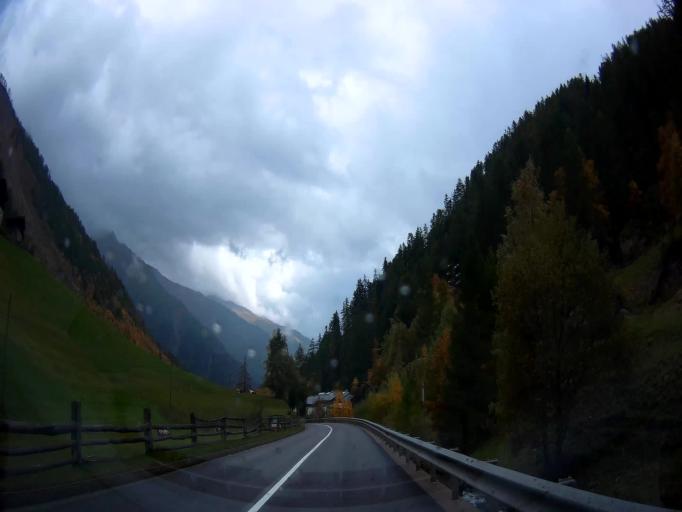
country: IT
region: Trentino-Alto Adige
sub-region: Bolzano
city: Senales
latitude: 46.7123
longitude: 10.8945
